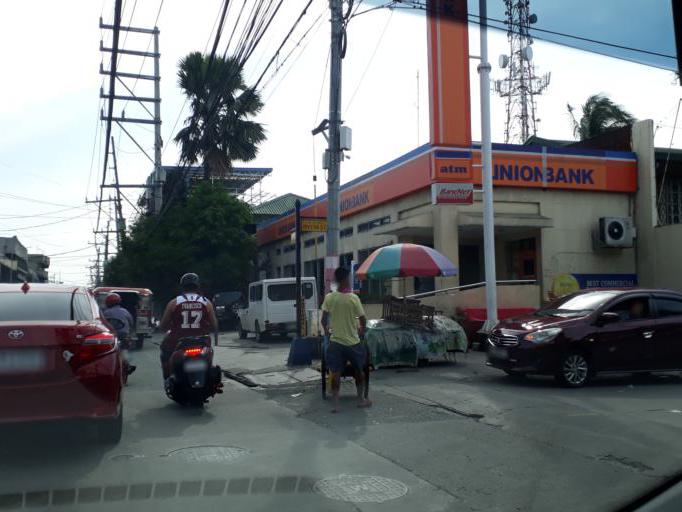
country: PH
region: Metro Manila
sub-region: Caloocan City
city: Niugan
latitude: 14.6697
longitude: 120.9702
